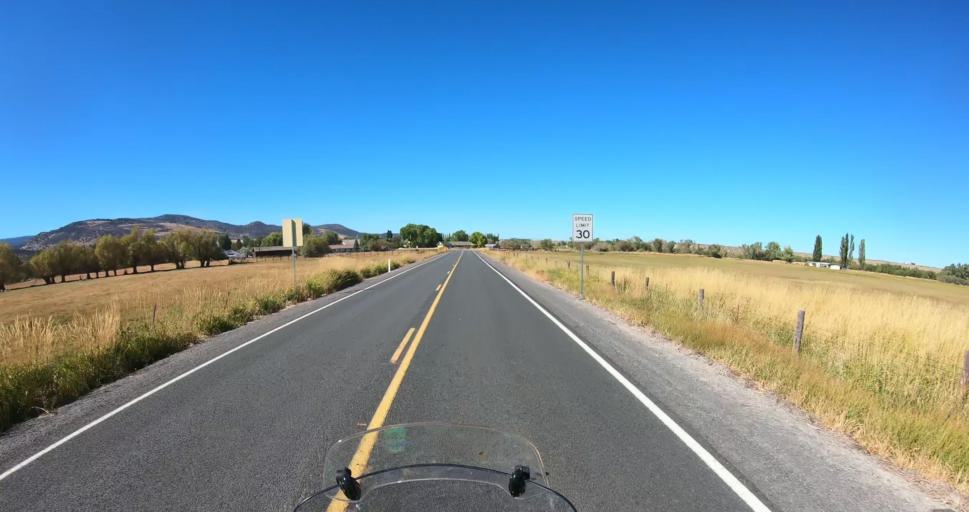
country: US
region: Oregon
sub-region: Lake County
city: Lakeview
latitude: 42.6916
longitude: -120.5367
